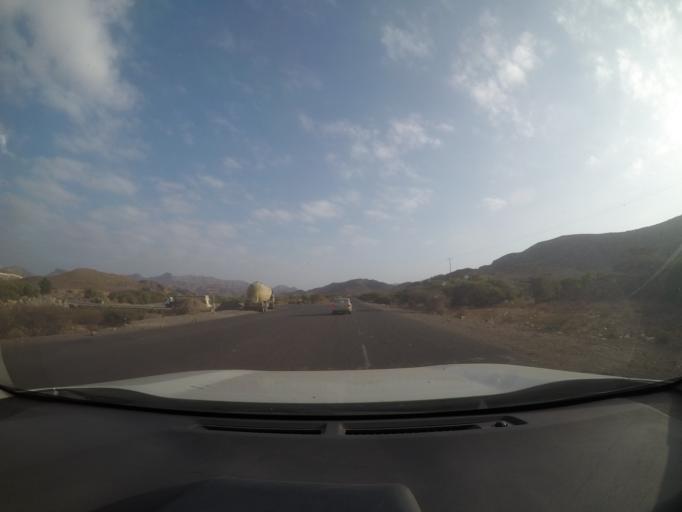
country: YE
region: Lahij
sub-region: Al Milah
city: Al Milah
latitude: 13.3336
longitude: 44.7592
